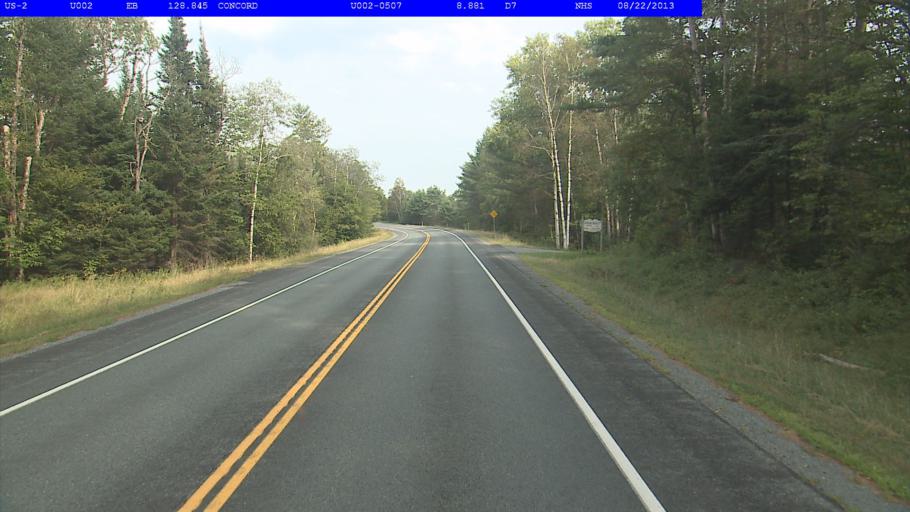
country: US
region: New Hampshire
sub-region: Grafton County
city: Littleton
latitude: 44.4499
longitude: -71.7990
